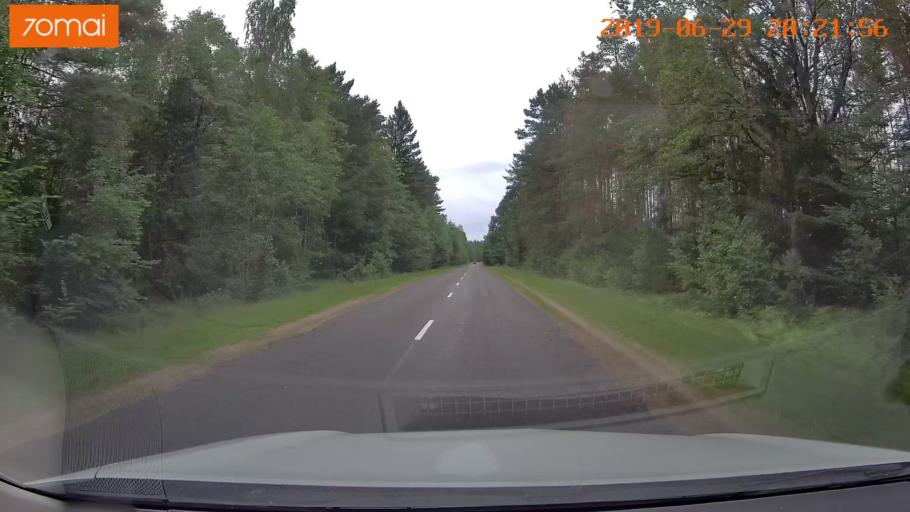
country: BY
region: Brest
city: Asnyezhytsy
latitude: 52.4256
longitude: 26.2534
